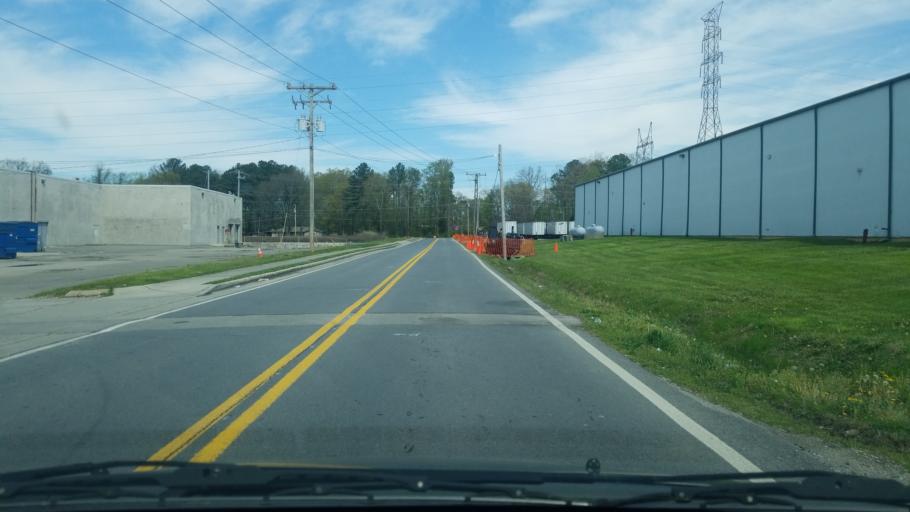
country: US
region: Georgia
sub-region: Catoosa County
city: Fort Oglethorpe
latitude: 34.9550
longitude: -85.2505
